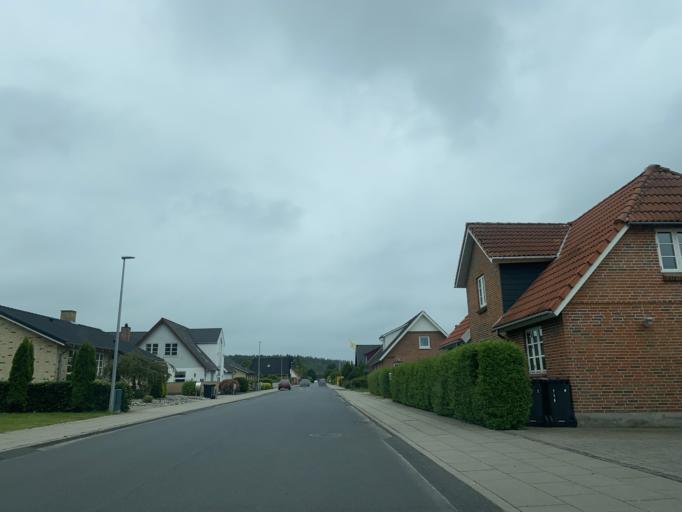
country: DK
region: Central Jutland
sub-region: Viborg Kommune
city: Bjerringbro
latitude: 56.3666
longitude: 9.6581
